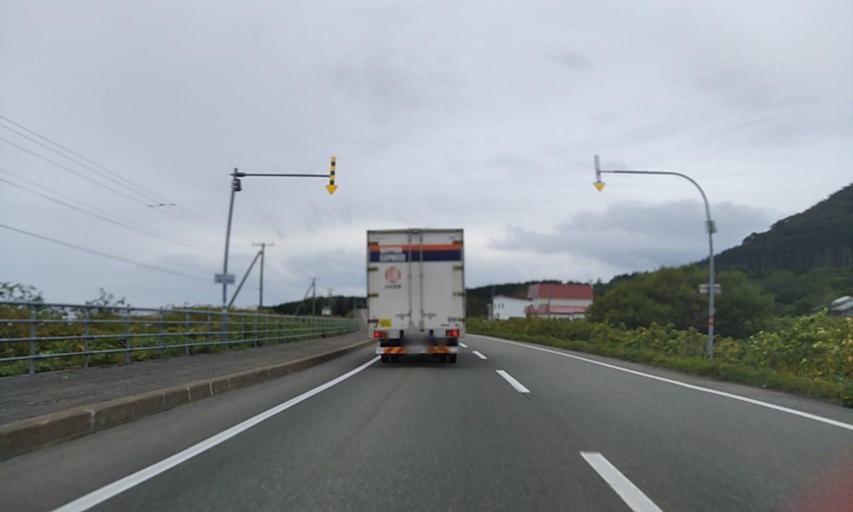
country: JP
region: Hokkaido
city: Nayoro
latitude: 45.0290
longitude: 142.5219
